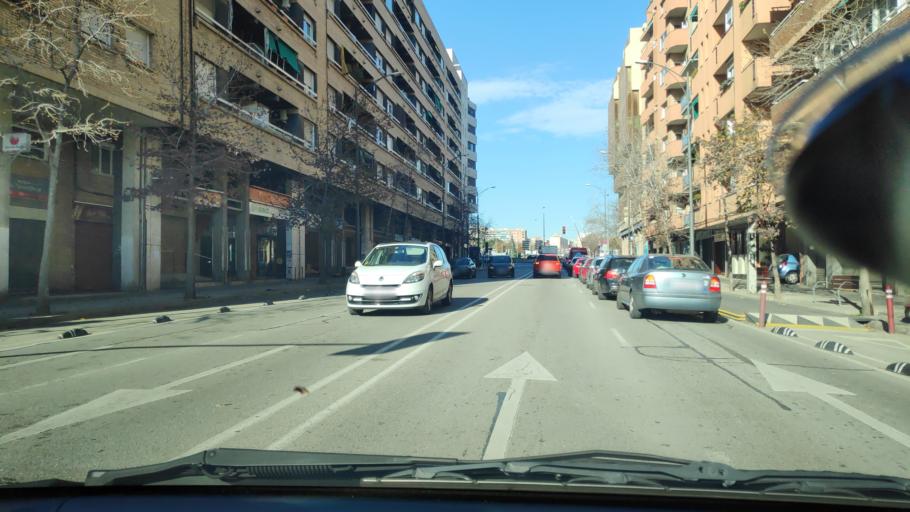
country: ES
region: Catalonia
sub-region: Provincia de Barcelona
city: Sabadell
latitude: 41.5486
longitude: 2.0988
